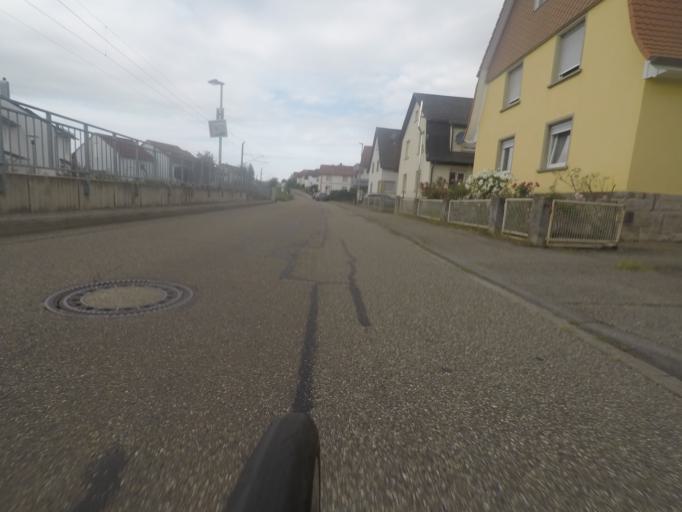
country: DE
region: Baden-Wuerttemberg
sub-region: Karlsruhe Region
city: Gaggenau
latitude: 48.7932
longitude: 8.3377
